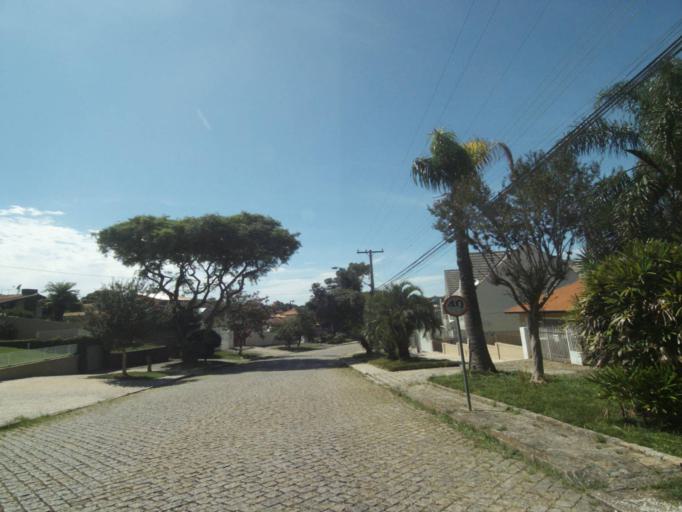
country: BR
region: Parana
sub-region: Curitiba
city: Curitiba
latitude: -25.4602
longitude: -49.2455
